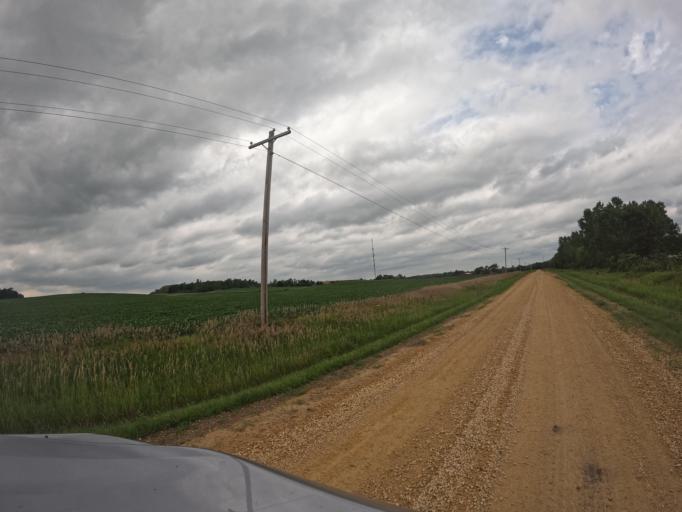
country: US
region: Iowa
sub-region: Clinton County
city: De Witt
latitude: 41.7986
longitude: -90.5683
